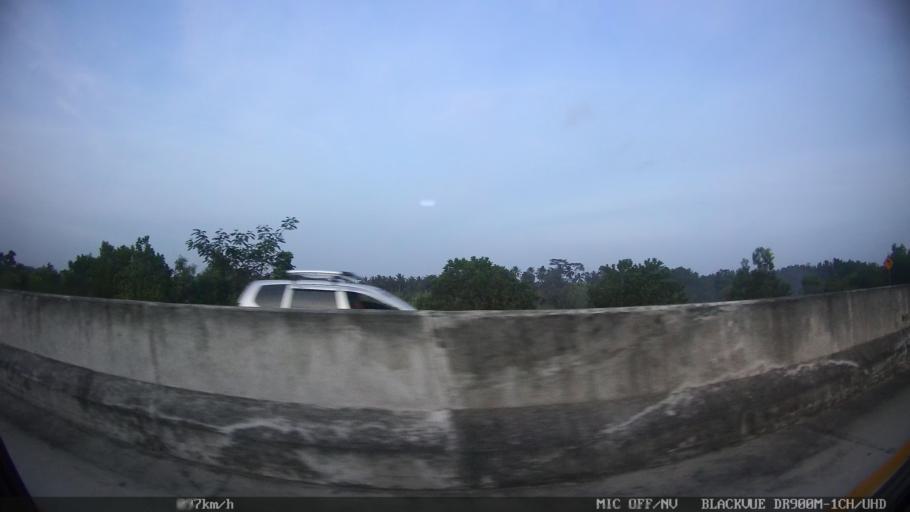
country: ID
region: Lampung
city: Penengahan
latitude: -5.7865
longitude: 105.7237
